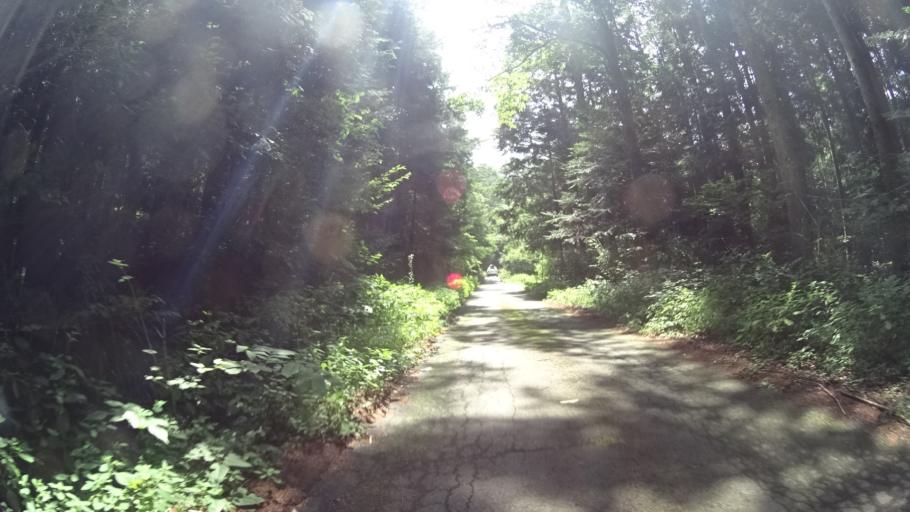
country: JP
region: Yamanashi
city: Nirasaki
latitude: 35.8884
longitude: 138.4759
